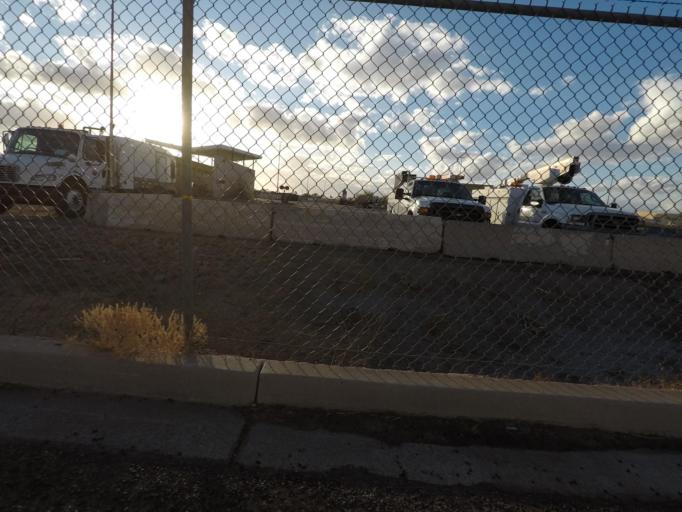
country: US
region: Arizona
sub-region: Maricopa County
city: Glendale
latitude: 33.4973
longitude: -112.1448
